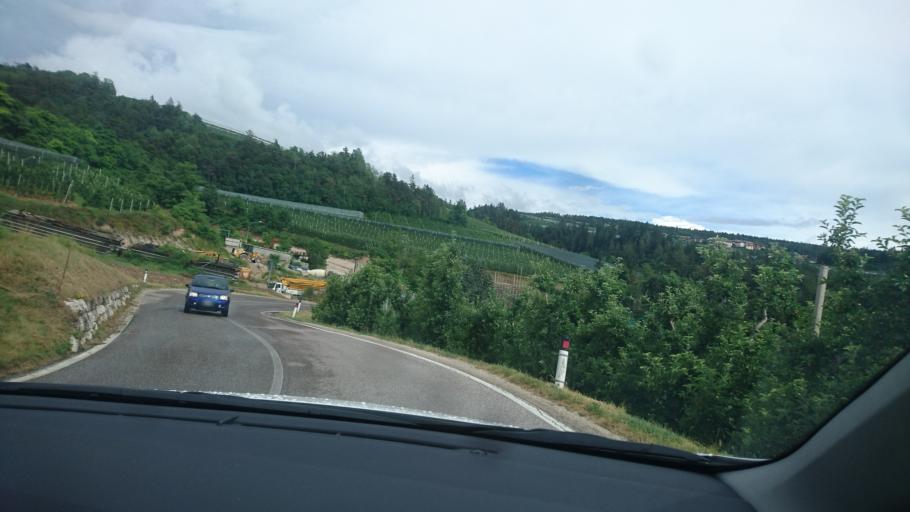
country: IT
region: Trentino-Alto Adige
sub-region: Provincia di Trento
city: Sanzeno
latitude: 46.3719
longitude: 11.0852
